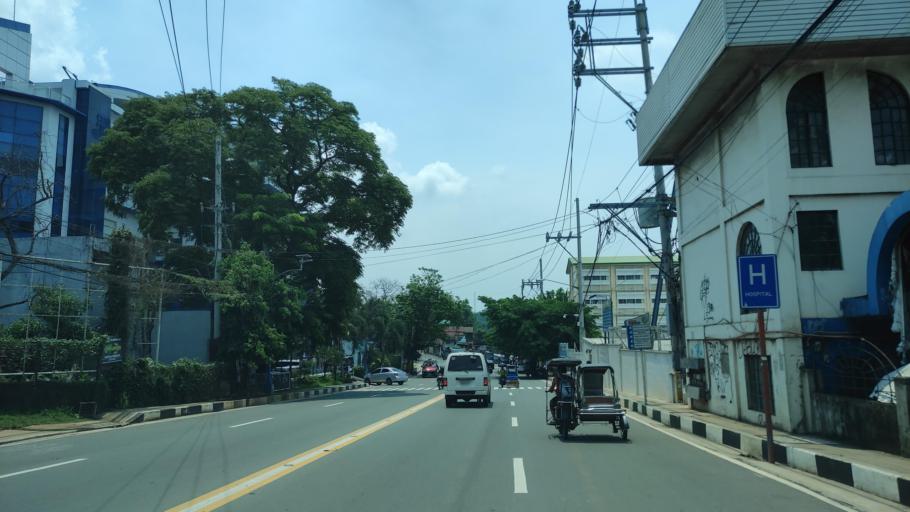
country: PH
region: Calabarzon
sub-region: Province of Rizal
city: Taytay
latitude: 14.5890
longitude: 121.1703
